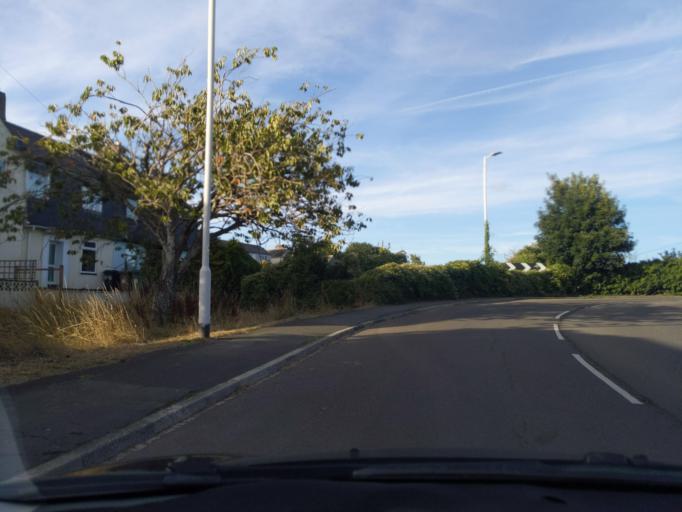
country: GB
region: England
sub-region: Plymouth
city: Plymstock
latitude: 50.3762
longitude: -4.1108
